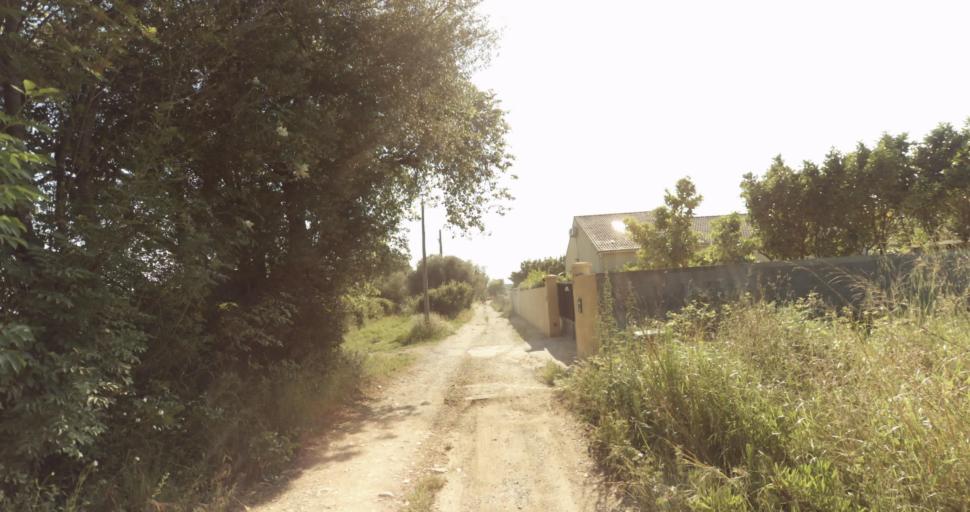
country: FR
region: Corsica
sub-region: Departement de la Haute-Corse
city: Biguglia
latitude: 42.6329
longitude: 9.4324
